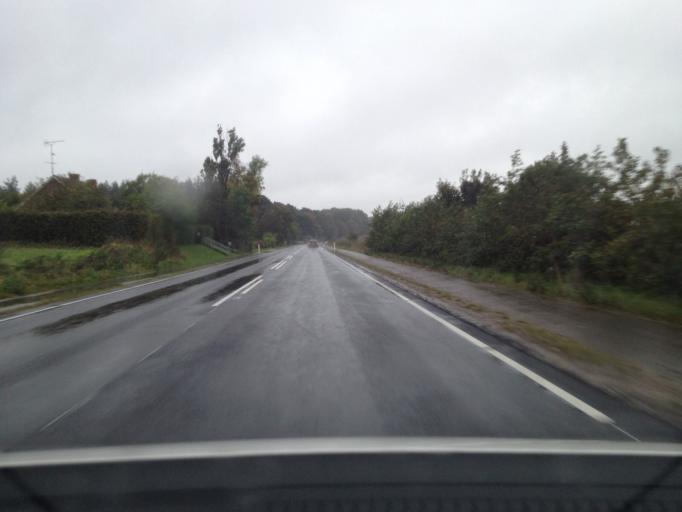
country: DK
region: Zealand
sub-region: Holbaek Kommune
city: Tollose
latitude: 55.5290
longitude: 11.7217
